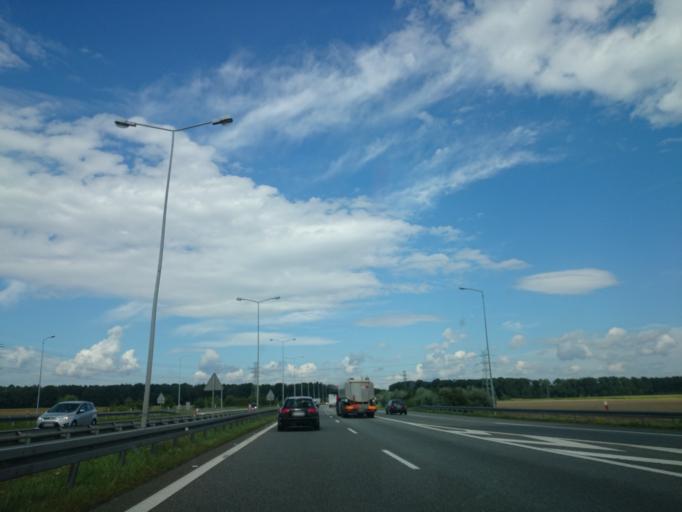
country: PL
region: Opole Voivodeship
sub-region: Powiat opolski
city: Proszkow
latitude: 50.5305
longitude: 17.9142
